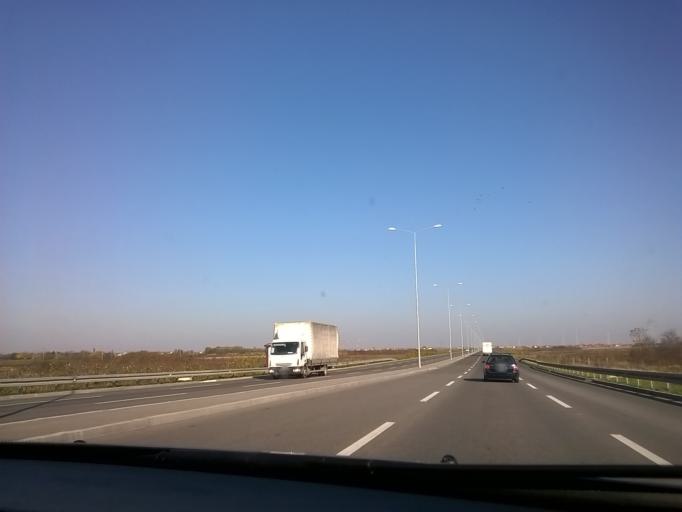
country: RS
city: Ovca
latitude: 44.8654
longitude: 20.5148
